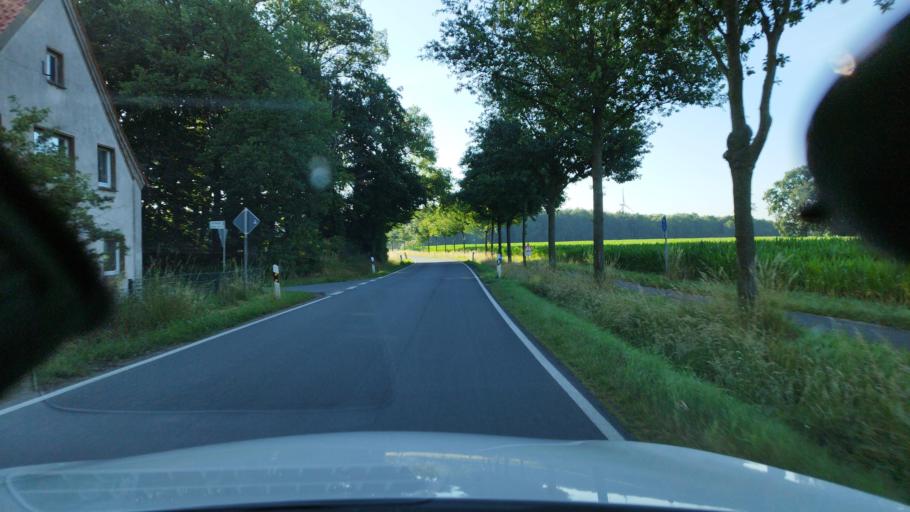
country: DE
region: North Rhine-Westphalia
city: Selm
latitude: 51.6703
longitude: 7.4302
